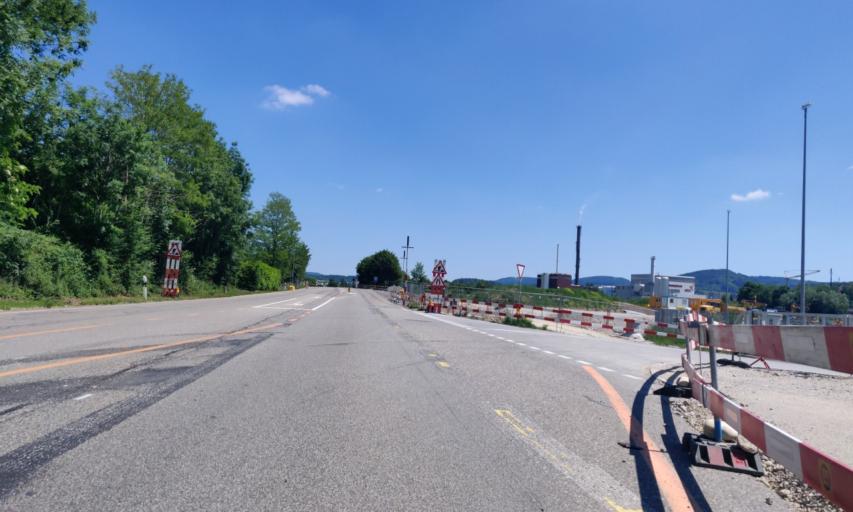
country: CH
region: Basel-Landschaft
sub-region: Bezirk Liestal
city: Pratteln
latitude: 47.5312
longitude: 7.6906
